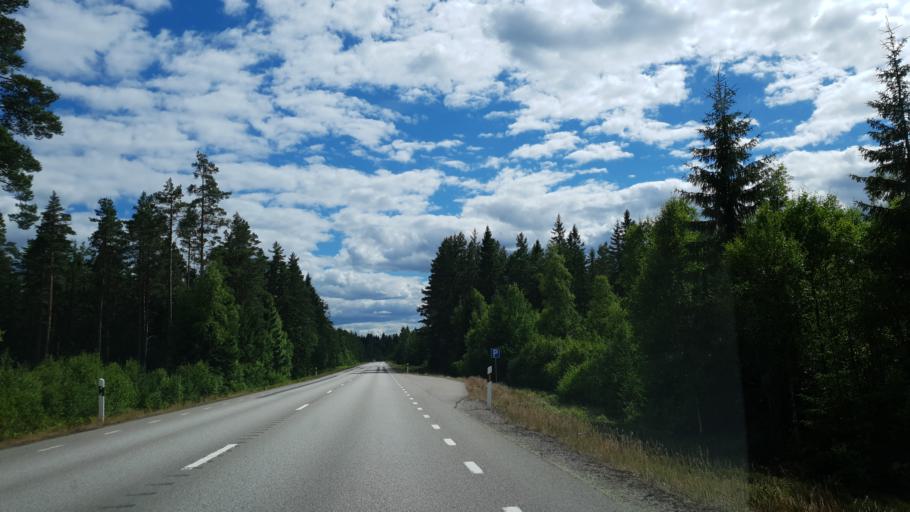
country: SE
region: Kronoberg
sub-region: Uppvidinge Kommun
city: Lenhovda
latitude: 56.9060
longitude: 15.3676
